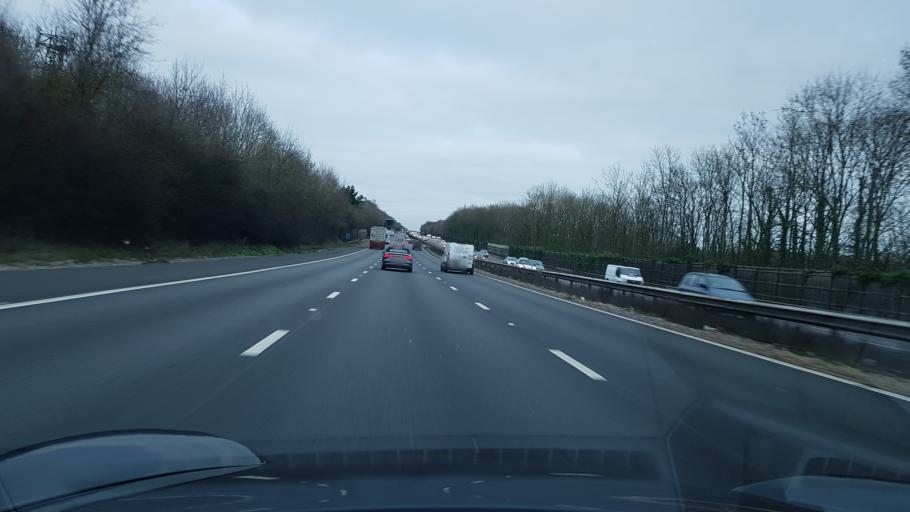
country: GB
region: England
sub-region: Hampshire
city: Compton
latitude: 51.0102
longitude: -1.3484
